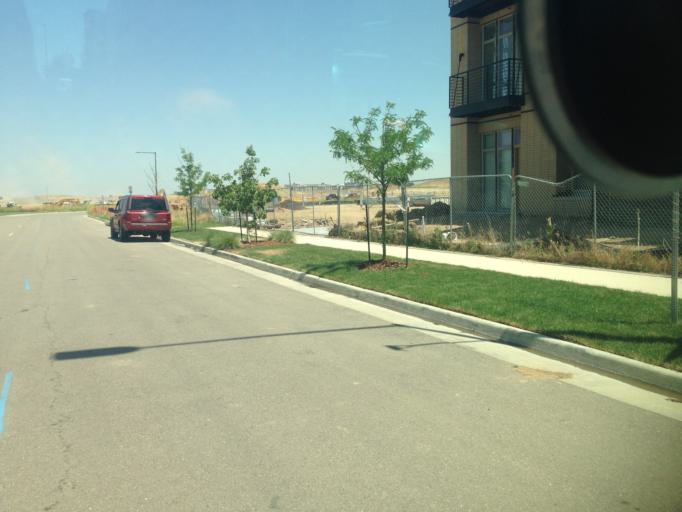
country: US
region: Colorado
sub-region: Adams County
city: Aurora
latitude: 39.8086
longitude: -104.7796
